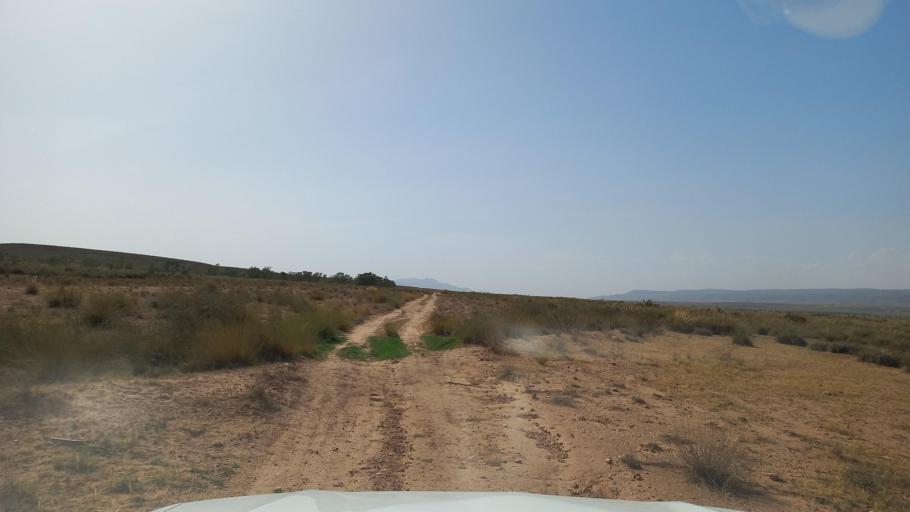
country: TN
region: Al Qasrayn
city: Kasserine
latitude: 35.2142
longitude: 9.0000
